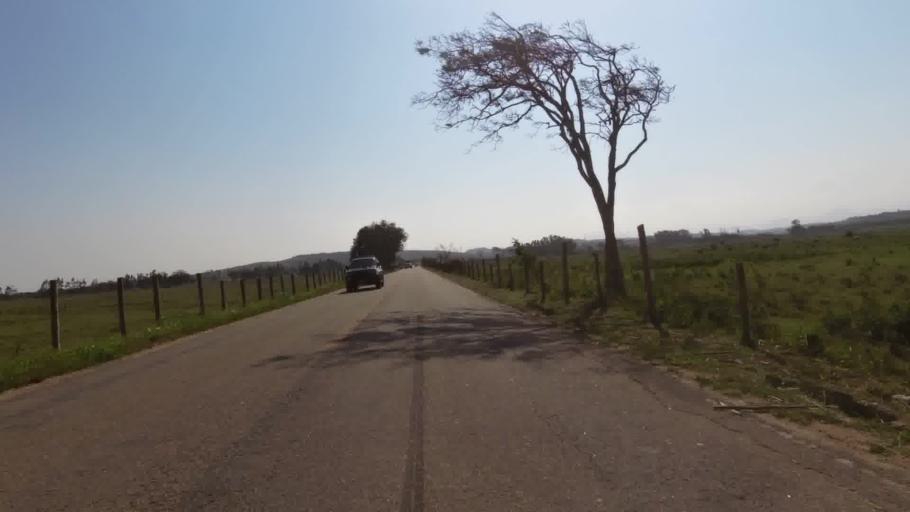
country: BR
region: Espirito Santo
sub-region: Itapemirim
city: Itapemirim
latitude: -20.9864
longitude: -40.8598
